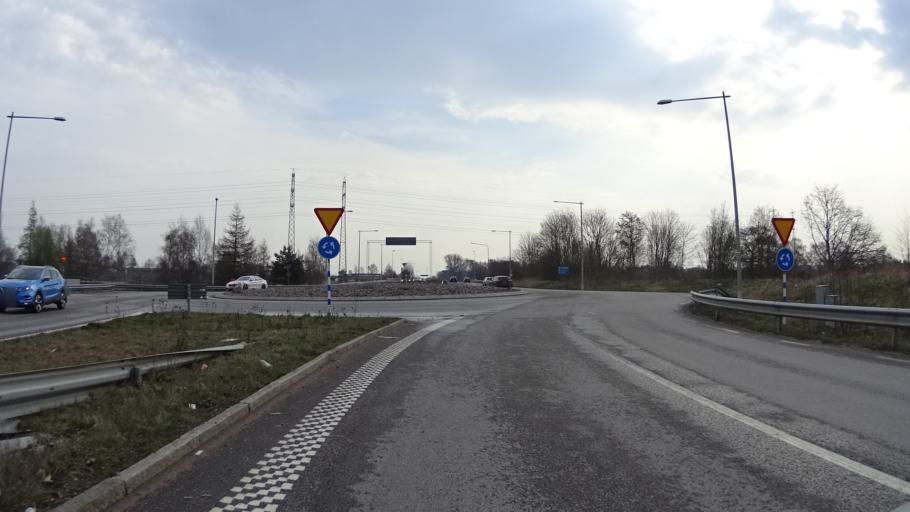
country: SE
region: Halland
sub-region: Halmstads Kommun
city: Fyllinge
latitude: 56.6736
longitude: 12.8953
